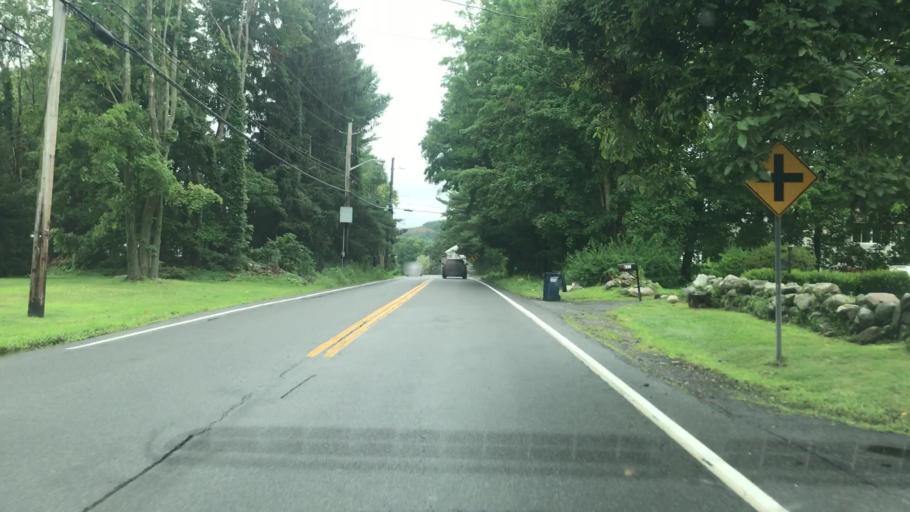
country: US
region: New York
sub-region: Westchester County
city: Jefferson Valley-Yorktown
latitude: 41.3505
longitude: -73.7802
